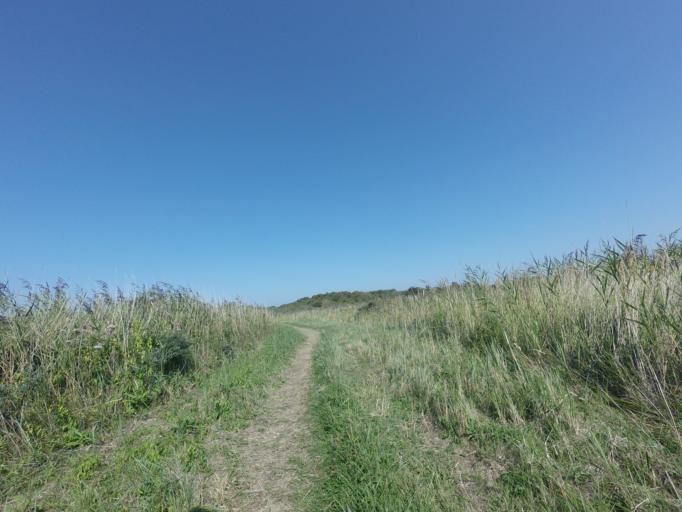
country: NL
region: Friesland
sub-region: Gemeente Schiermonnikoog
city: Schiermonnikoog
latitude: 53.4951
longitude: 6.2434
